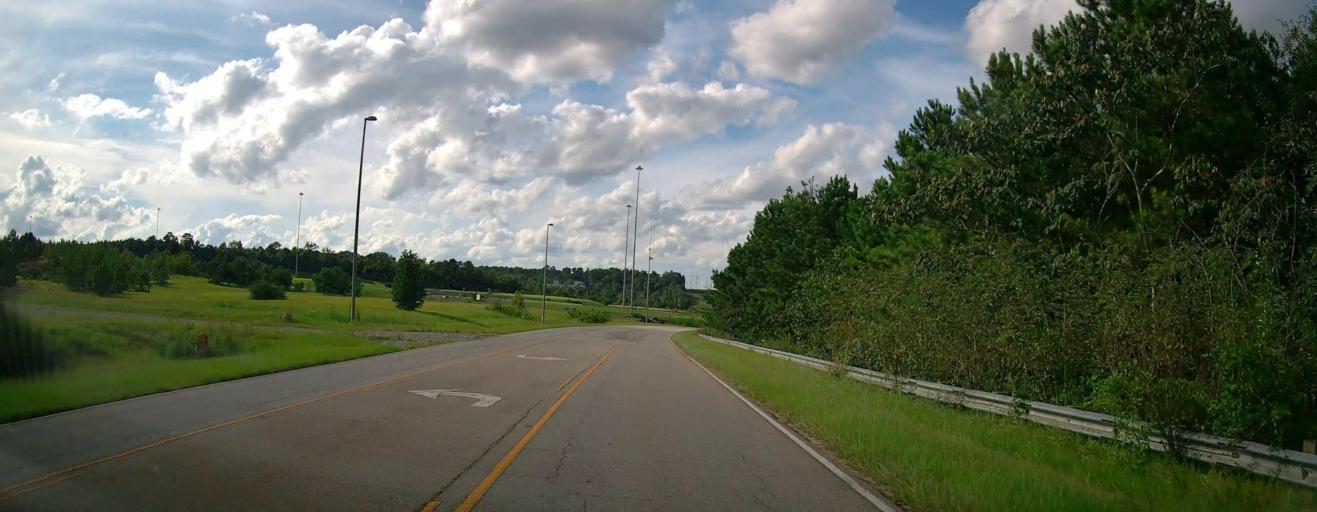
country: US
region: Alabama
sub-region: Russell County
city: Phenix City
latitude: 32.5023
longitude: -85.0021
